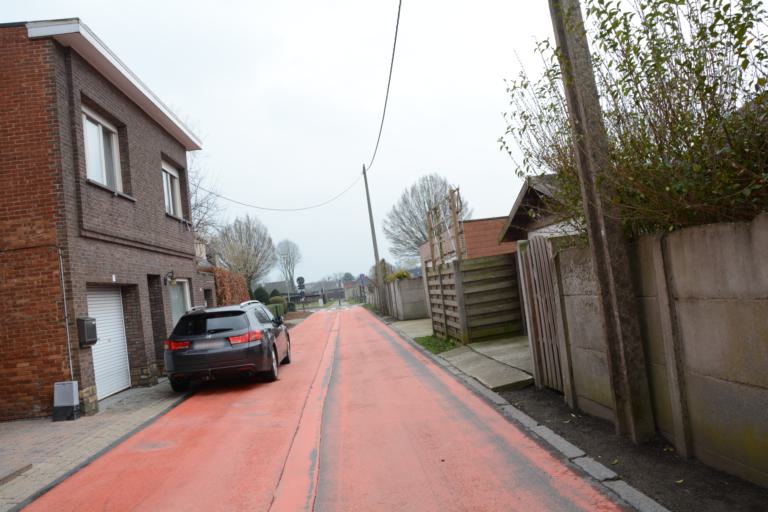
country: BE
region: Flanders
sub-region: Provincie Antwerpen
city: Herenthout
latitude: 51.1371
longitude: 4.7585
